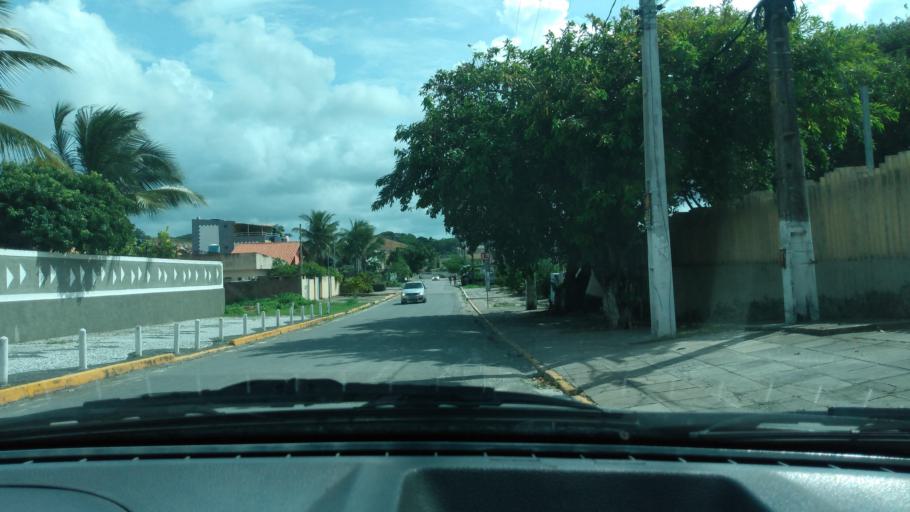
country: BR
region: Pernambuco
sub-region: Cabo De Santo Agostinho
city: Cabo
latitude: -8.3318
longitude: -34.9514
